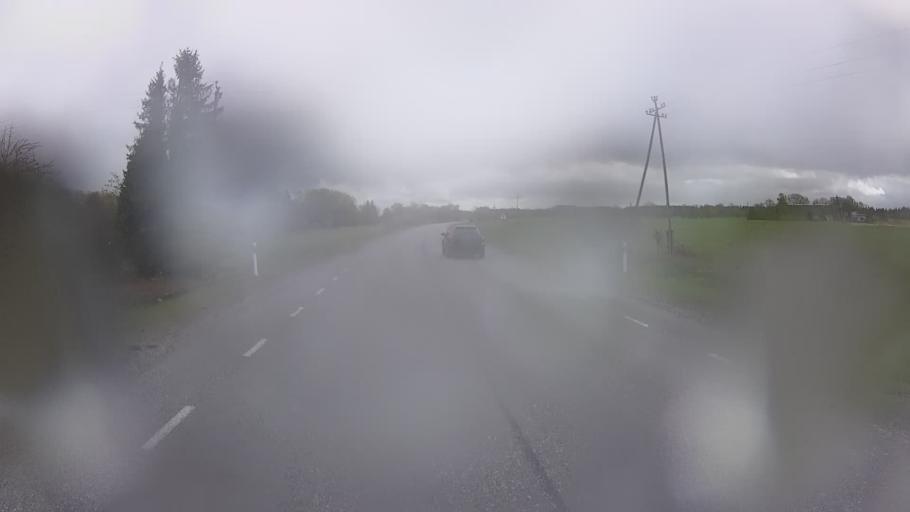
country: EE
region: Hiiumaa
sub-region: Kaerdla linn
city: Kardla
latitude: 58.8353
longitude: 22.7933
